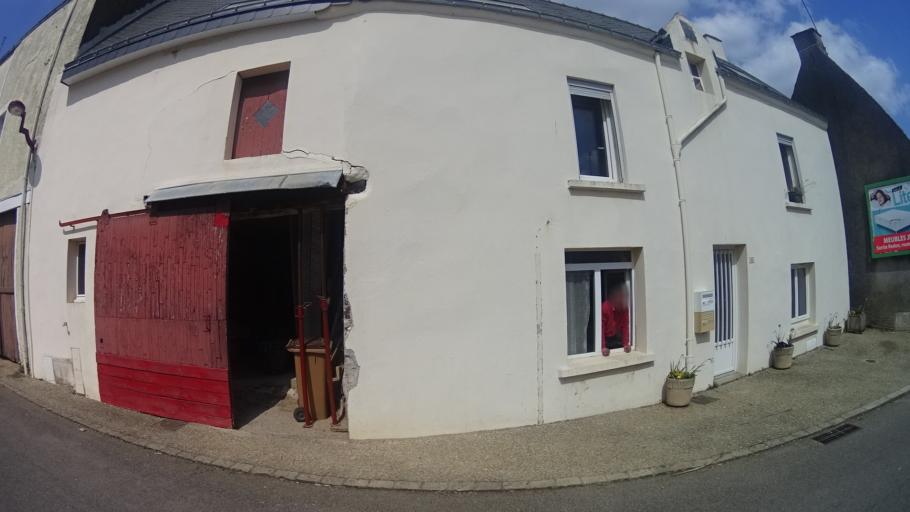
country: FR
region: Brittany
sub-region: Departement du Morbihan
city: Beganne
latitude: 47.5965
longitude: -2.2383
